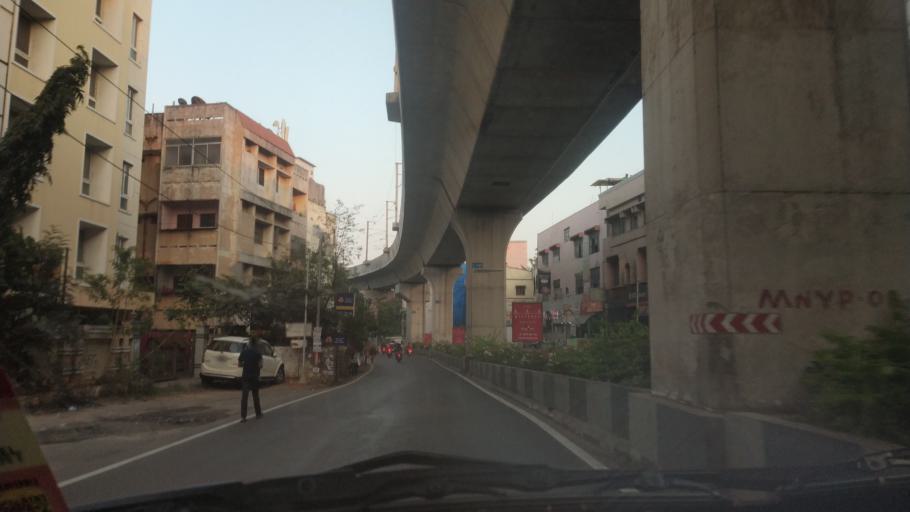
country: IN
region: Telangana
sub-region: Rangareddi
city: Kukatpalli
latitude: 17.4371
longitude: 78.4363
